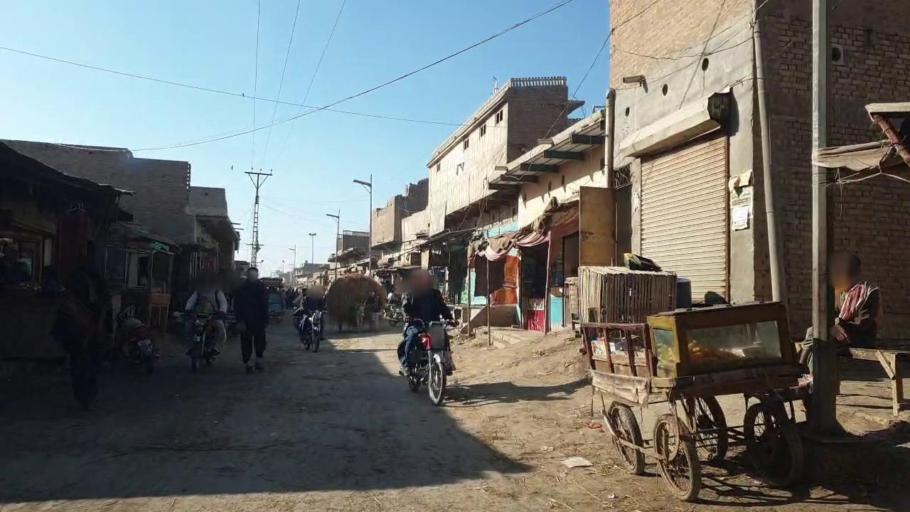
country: PK
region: Sindh
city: New Badah
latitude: 27.3282
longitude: 68.0272
